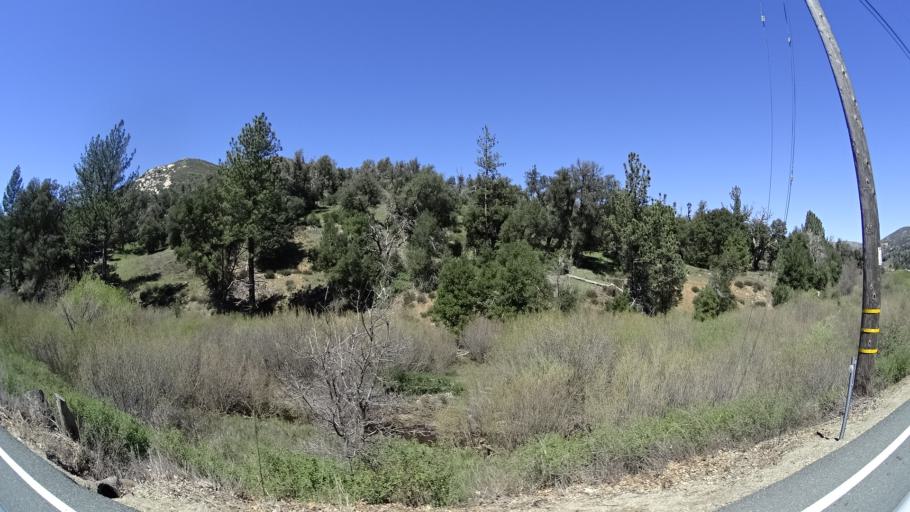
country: US
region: California
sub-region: San Diego County
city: Descanso
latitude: 32.9089
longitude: -116.5770
